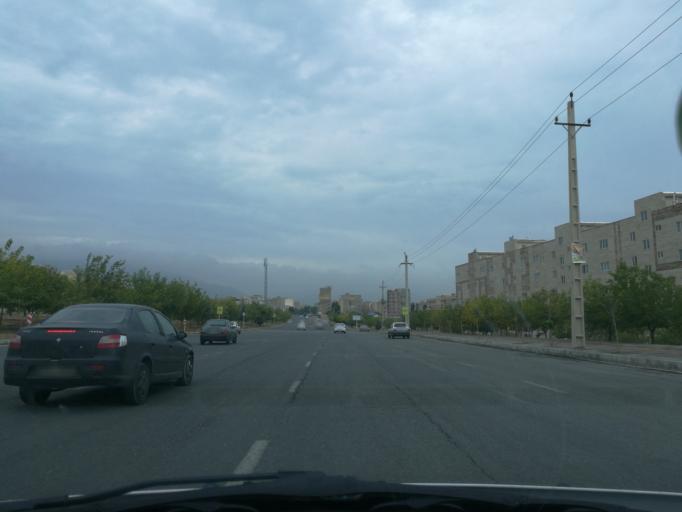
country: IR
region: Alborz
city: Karaj
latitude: 35.8632
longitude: 50.9316
